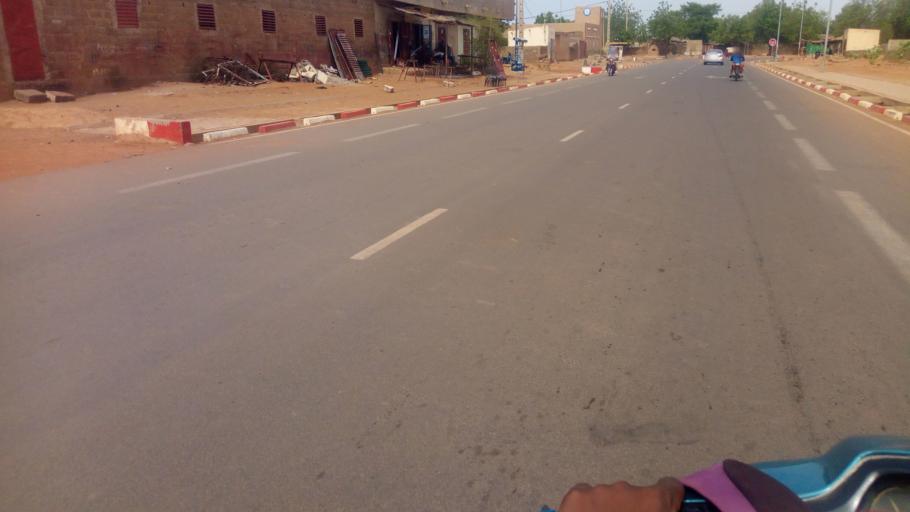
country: ML
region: Segou
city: Segou
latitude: 13.4280
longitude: -6.2863
